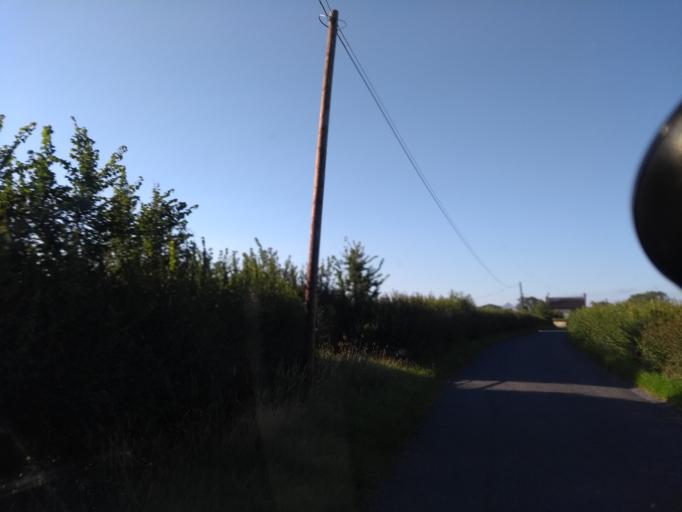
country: GB
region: England
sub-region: Somerset
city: Axbridge
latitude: 51.2643
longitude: -2.8671
